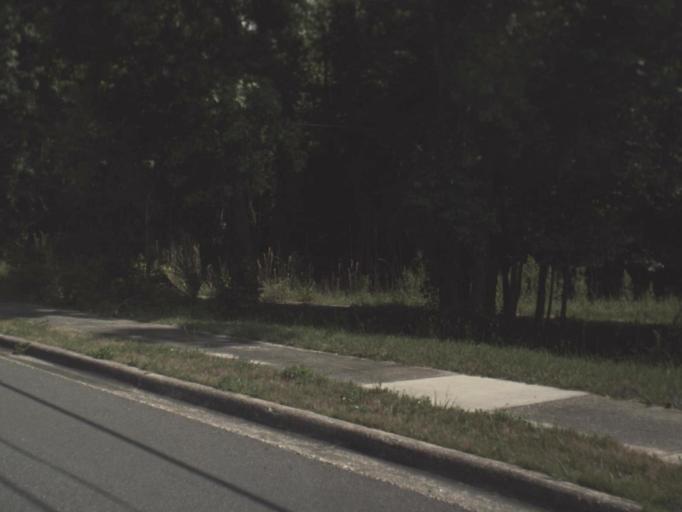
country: US
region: Florida
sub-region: Alachua County
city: Waldo
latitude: 29.7802
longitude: -82.1666
